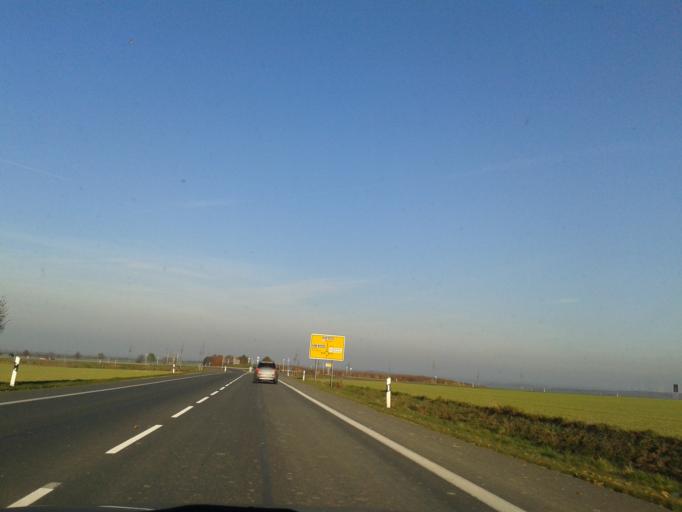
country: DE
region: North Rhine-Westphalia
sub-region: Regierungsbezirk Detmold
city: Buren
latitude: 51.5681
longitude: 8.5399
